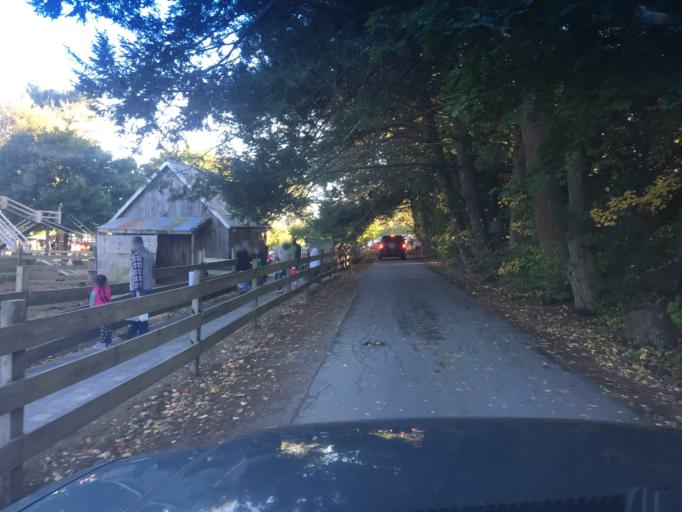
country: US
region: Massachusetts
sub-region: Middlesex County
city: Stow
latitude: 42.4116
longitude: -71.5138
